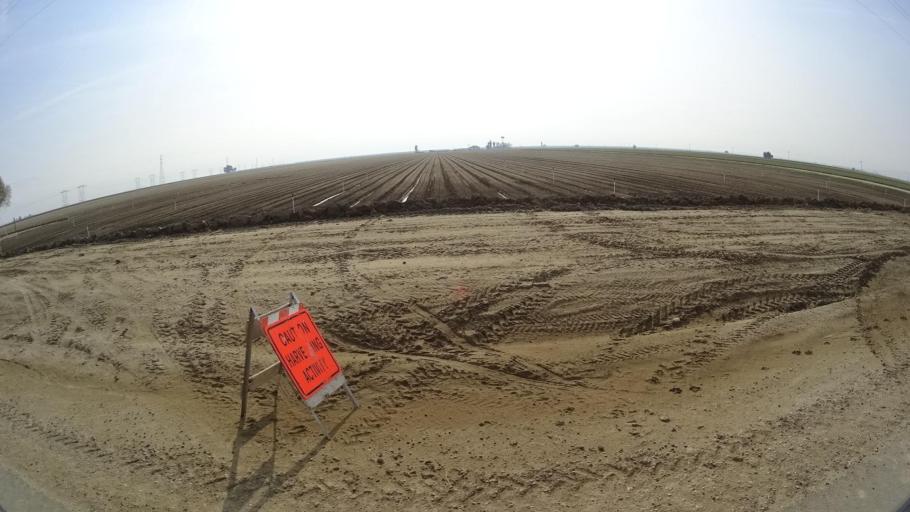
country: US
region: California
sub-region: Kern County
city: Arvin
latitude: 35.0455
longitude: -118.8779
